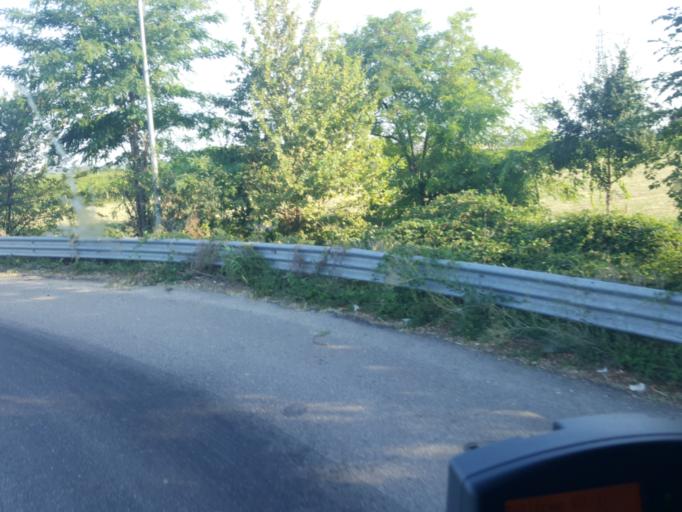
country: IT
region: Emilia-Romagna
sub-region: Provincia di Modena
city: San Vito
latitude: 44.5335
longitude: 10.9853
